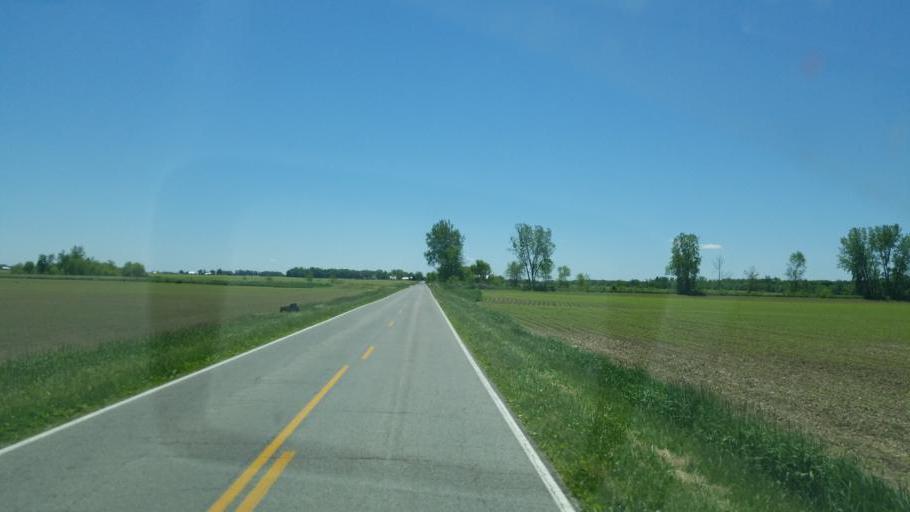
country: US
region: Indiana
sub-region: Randolph County
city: Union City
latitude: 40.2942
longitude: -84.8039
